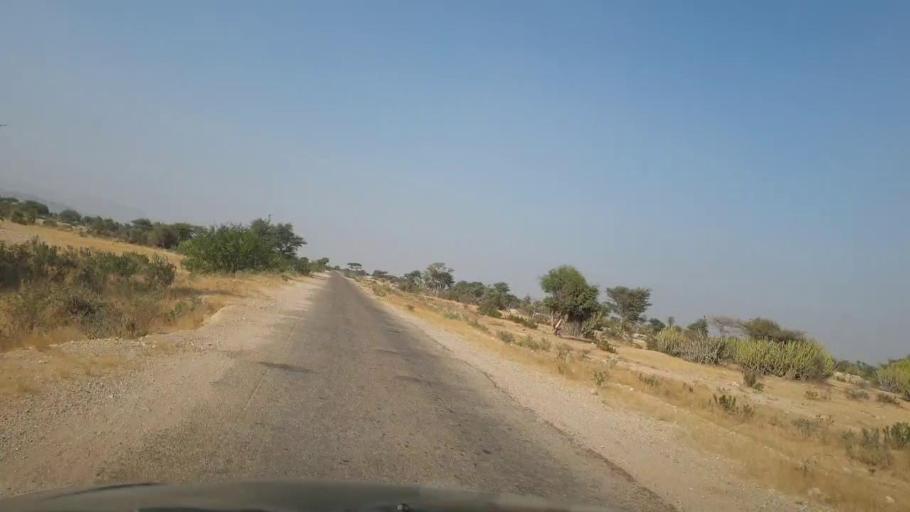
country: PK
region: Sindh
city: Jamshoro
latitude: 25.5653
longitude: 67.8254
